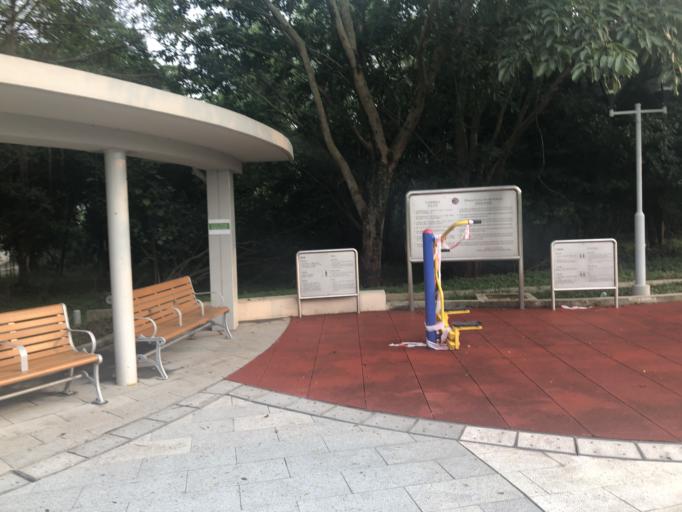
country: CN
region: Guangdong
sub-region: Shenzhen
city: Shenzhen
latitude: 22.4854
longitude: 114.1027
